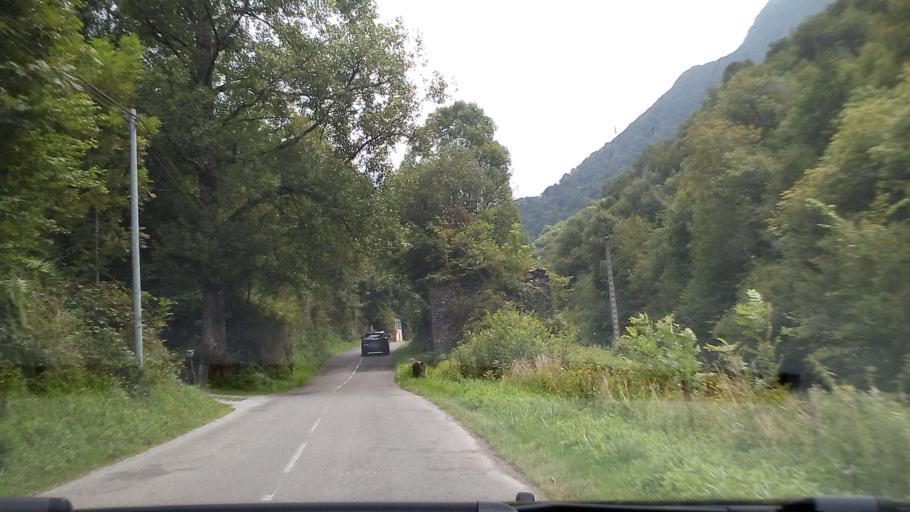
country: FR
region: Aquitaine
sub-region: Departement des Pyrenees-Atlantiques
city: Oloron-Sainte-Marie
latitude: 43.0783
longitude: -0.5933
